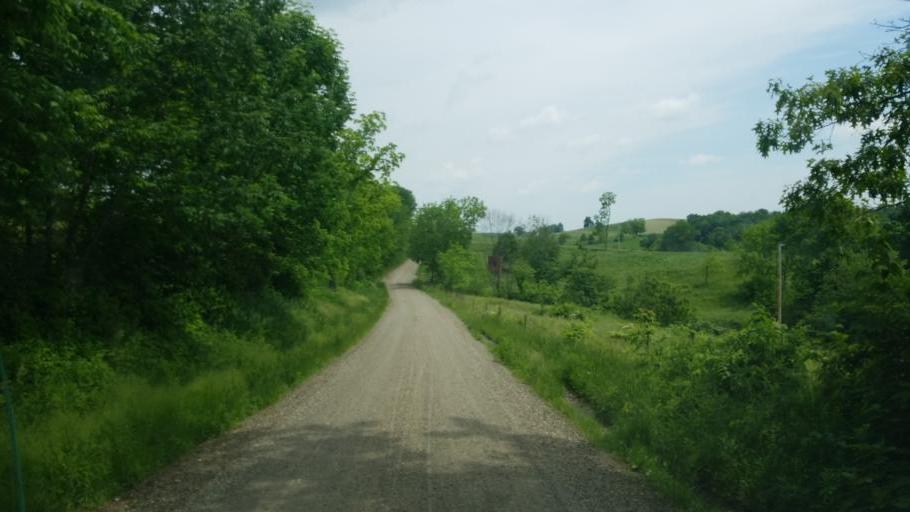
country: US
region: Ohio
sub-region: Holmes County
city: Millersburg
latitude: 40.4835
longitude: -81.8026
